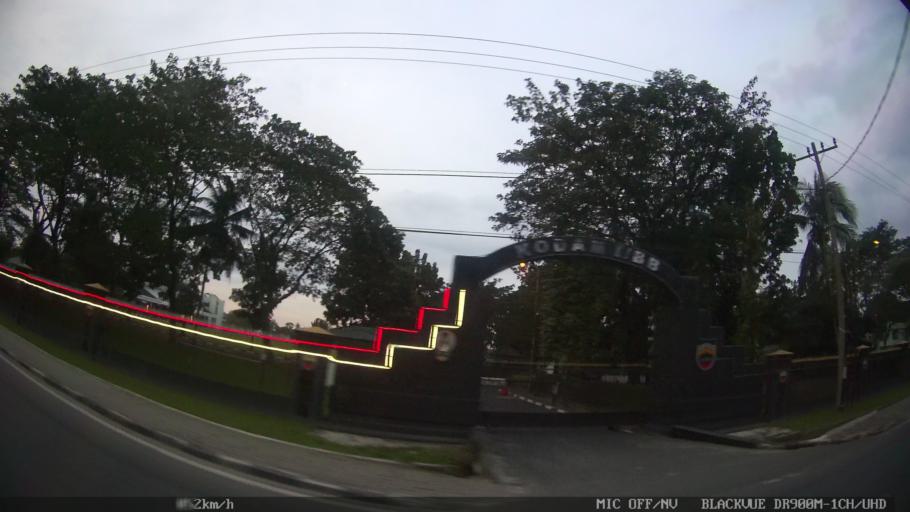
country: ID
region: North Sumatra
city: Sunggal
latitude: 3.5925
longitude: 98.6228
